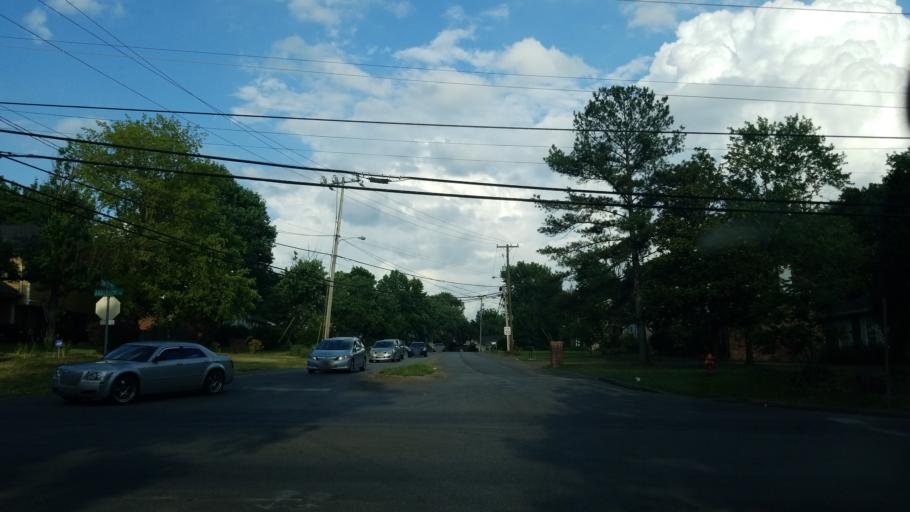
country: US
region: Tennessee
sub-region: Rutherford County
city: La Vergne
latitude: 36.0780
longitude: -86.6072
